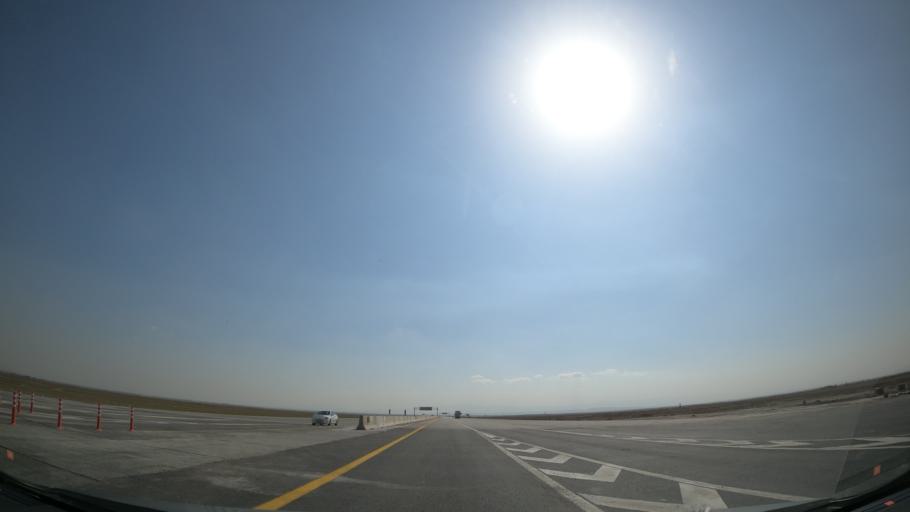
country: IR
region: Qazvin
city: Abyek
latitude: 35.9581
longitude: 50.4647
